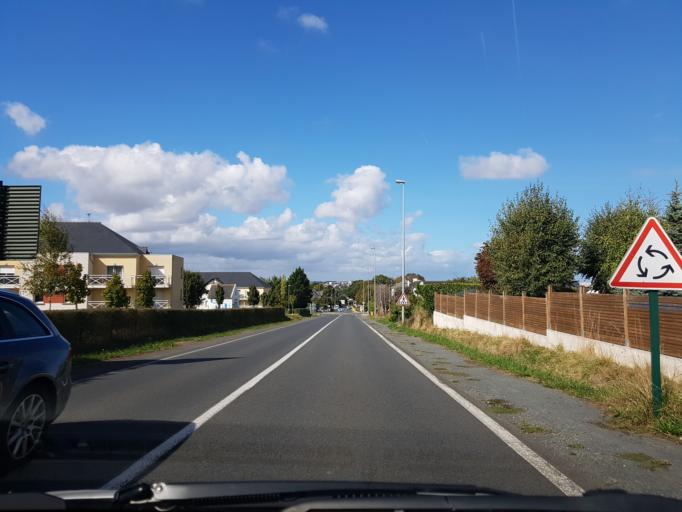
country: FR
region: Brittany
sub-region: Departement des Cotes-d'Armor
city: Langueux
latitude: 48.4849
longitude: -2.7493
